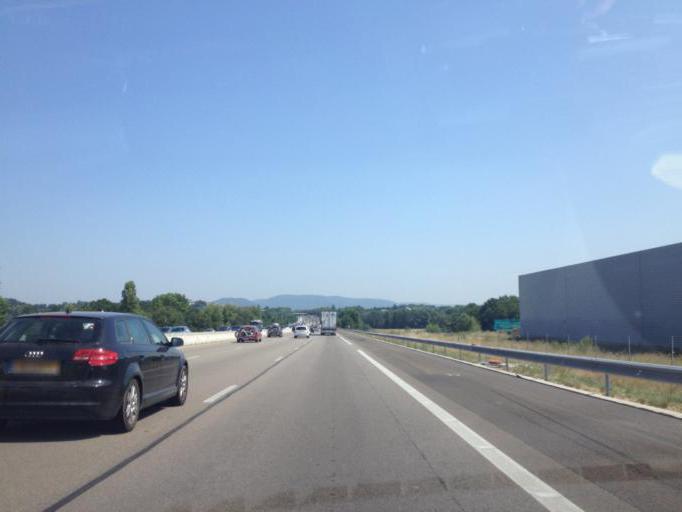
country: FR
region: Rhone-Alpes
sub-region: Departement de la Drome
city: Montboucher-sur-Jabron
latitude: 44.5388
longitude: 4.8054
